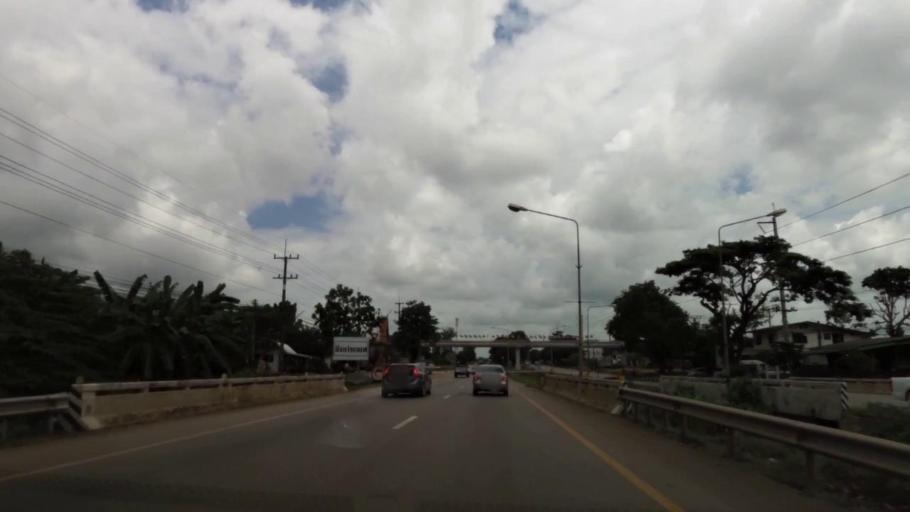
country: TH
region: Chanthaburi
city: Na Yai Am
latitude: 12.7847
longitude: 101.7946
